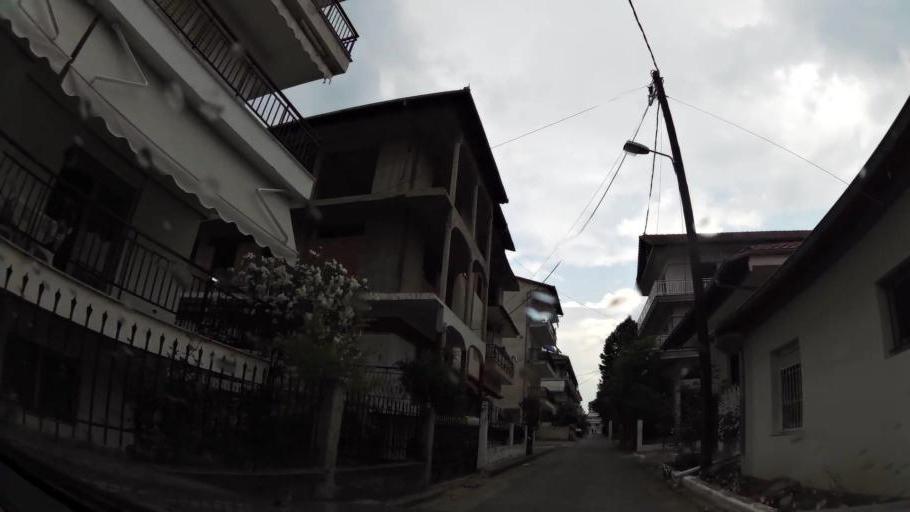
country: GR
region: Central Macedonia
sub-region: Nomos Imathias
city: Veroia
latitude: 40.5292
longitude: 22.1953
